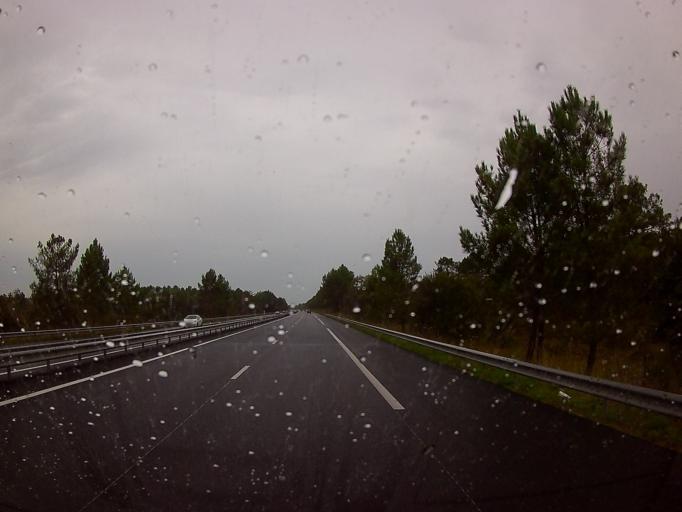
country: FR
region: Aquitaine
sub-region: Departement de la Dordogne
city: Saint-Medard-de-Mussidan
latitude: 45.0092
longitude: 0.2992
